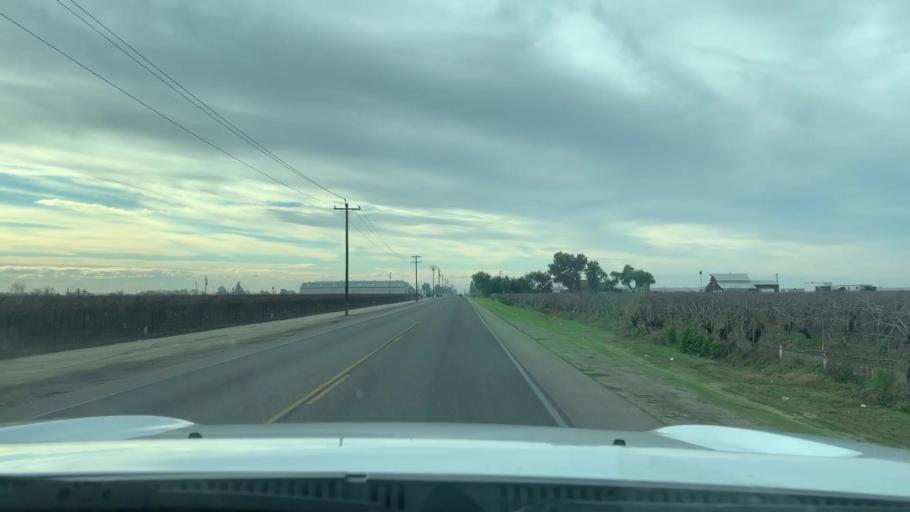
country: US
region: California
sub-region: Fresno County
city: Fowler
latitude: 36.6055
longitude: -119.7375
